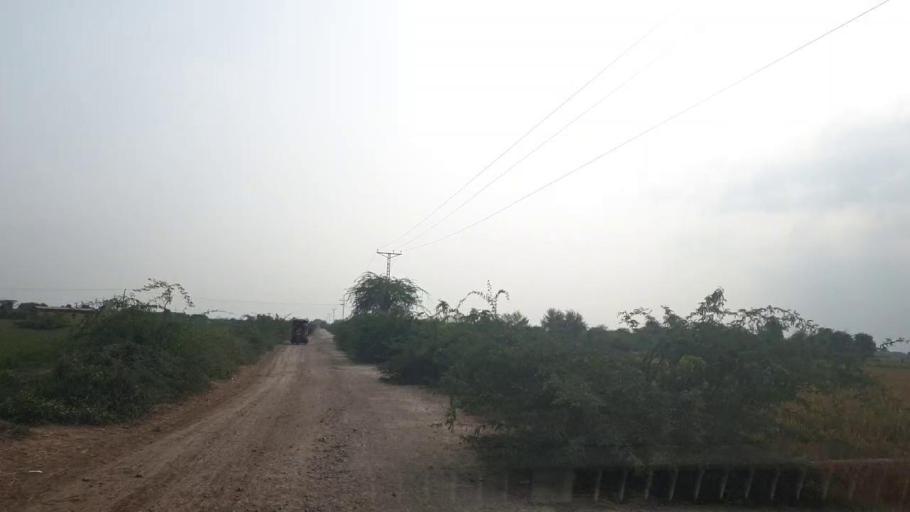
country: PK
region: Sindh
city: Badin
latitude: 24.6198
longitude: 68.6877
